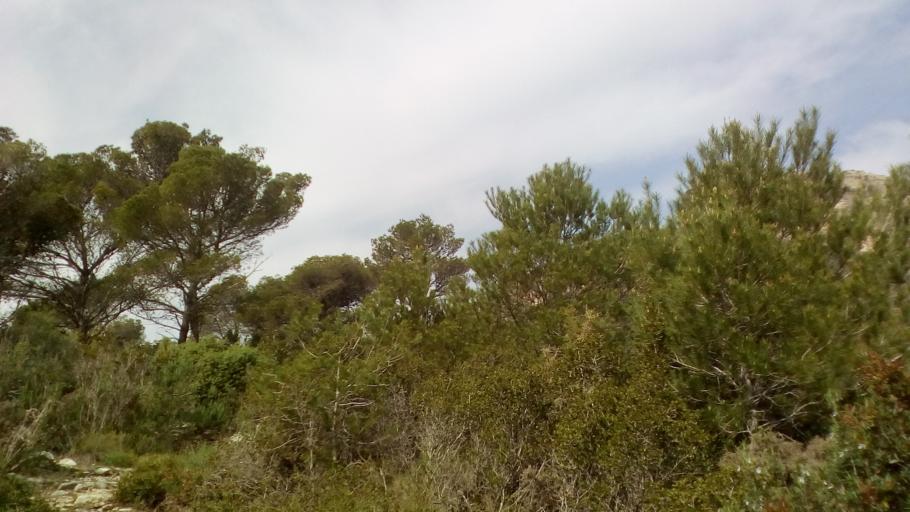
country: ES
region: Valencia
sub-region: Provincia de Valencia
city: Xeraco,Jaraco
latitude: 39.0376
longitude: -0.2361
